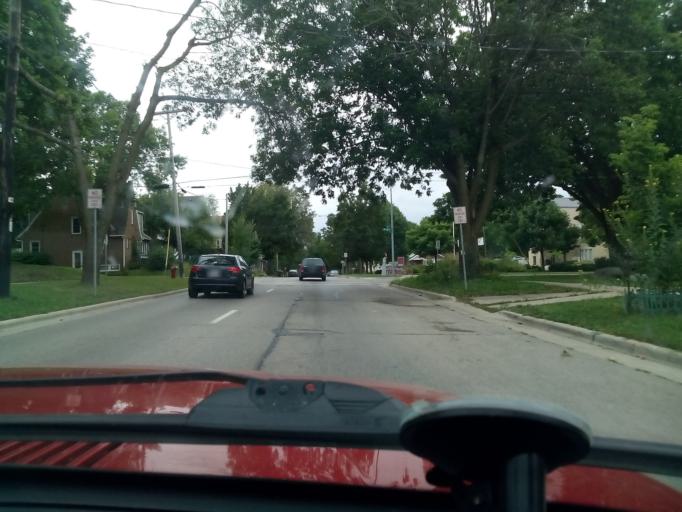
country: US
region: Wisconsin
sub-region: Dane County
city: Madison
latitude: 43.0867
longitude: -89.3748
